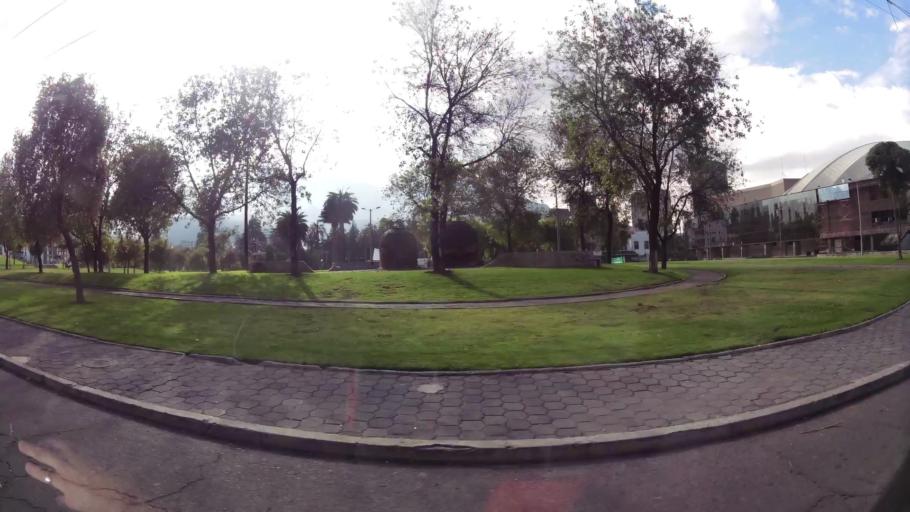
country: EC
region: Pichincha
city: Quito
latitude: -0.2115
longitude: -78.4958
